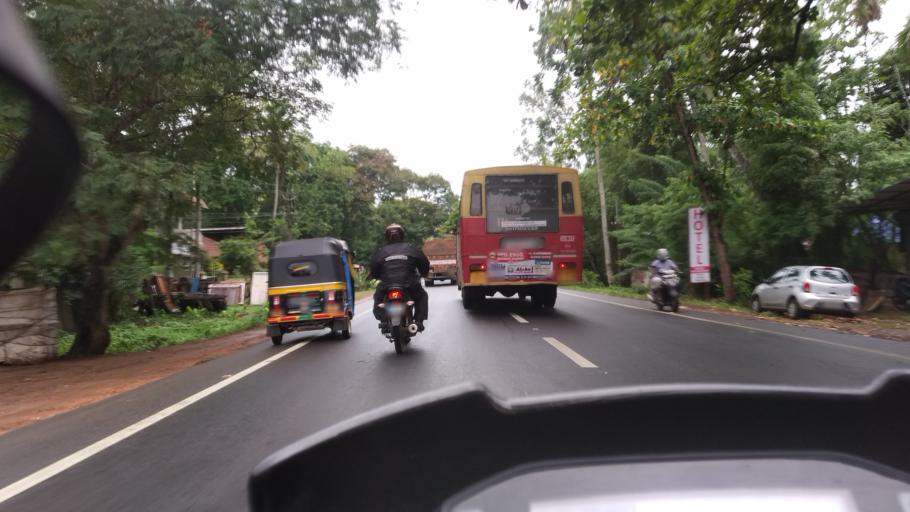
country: IN
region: Kerala
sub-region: Alappuzha
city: Mavelikara
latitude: 9.2909
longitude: 76.4361
